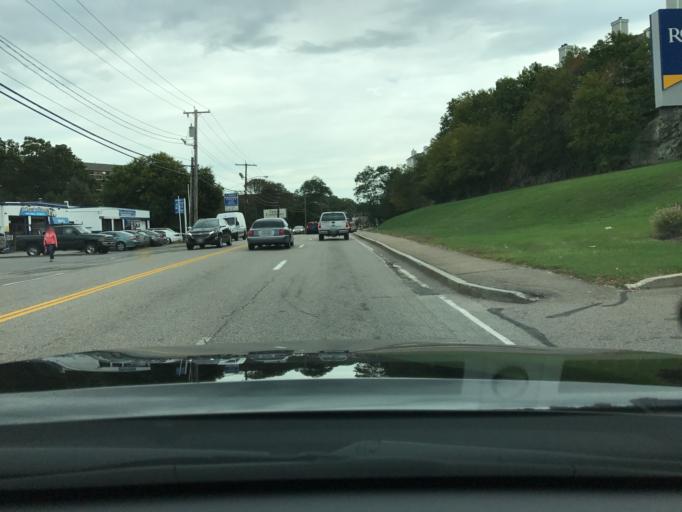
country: US
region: Massachusetts
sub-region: Norfolk County
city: Quincy
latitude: 42.2405
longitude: -70.9878
